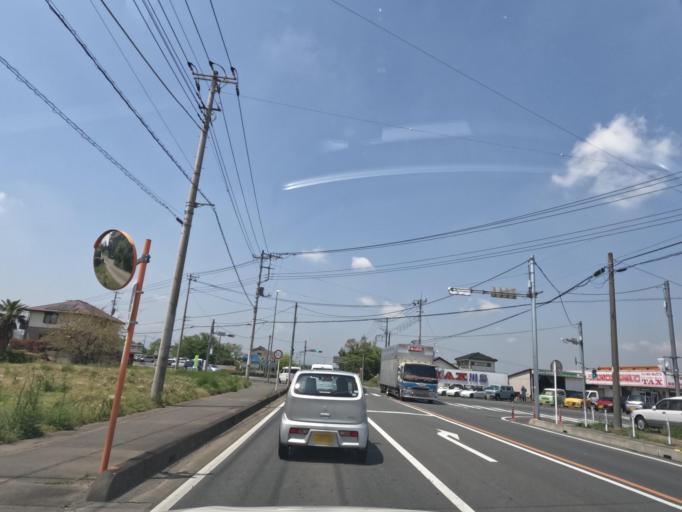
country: JP
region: Saitama
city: Kawagoe
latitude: 35.9643
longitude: 139.4926
